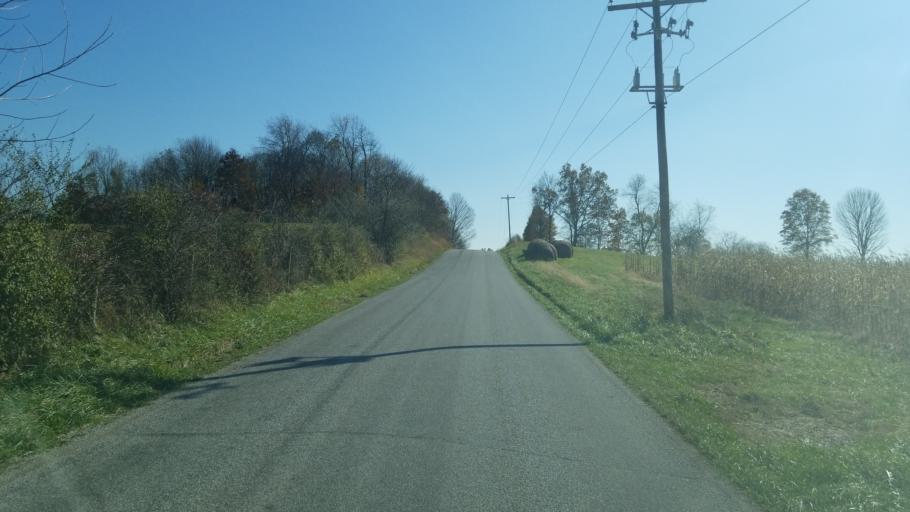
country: US
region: Ohio
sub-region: Licking County
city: Newark
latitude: 40.1258
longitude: -82.3893
